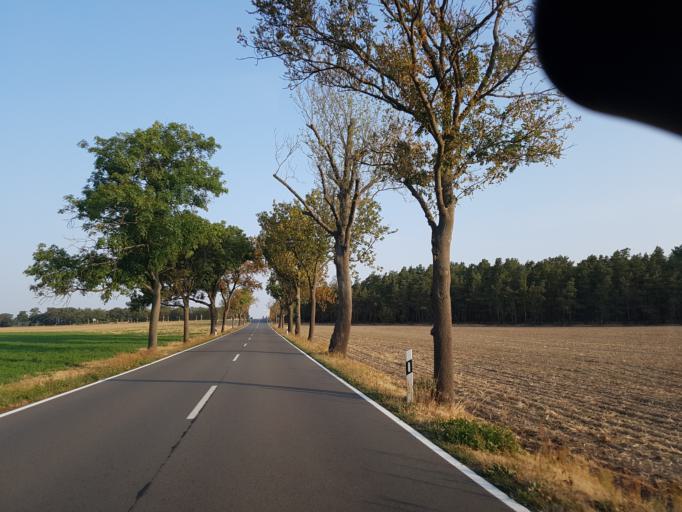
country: DE
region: Saxony-Anhalt
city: Pretzsch
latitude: 51.7402
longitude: 12.7586
